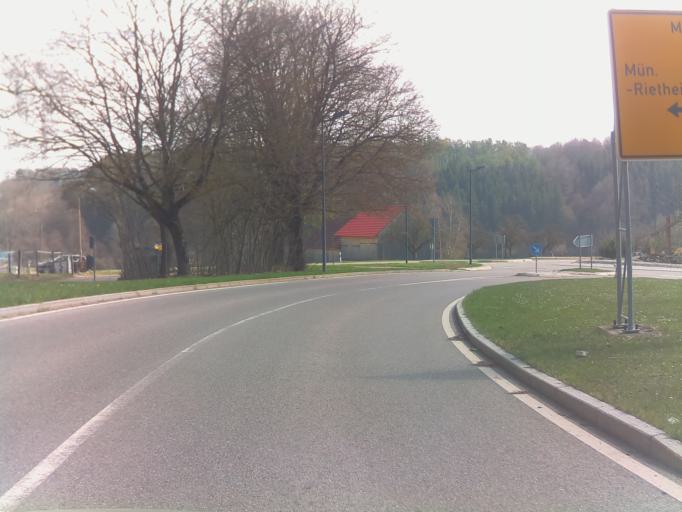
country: DE
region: Baden-Wuerttemberg
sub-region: Tuebingen Region
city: Gomadingen
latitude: 48.4235
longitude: 9.4400
